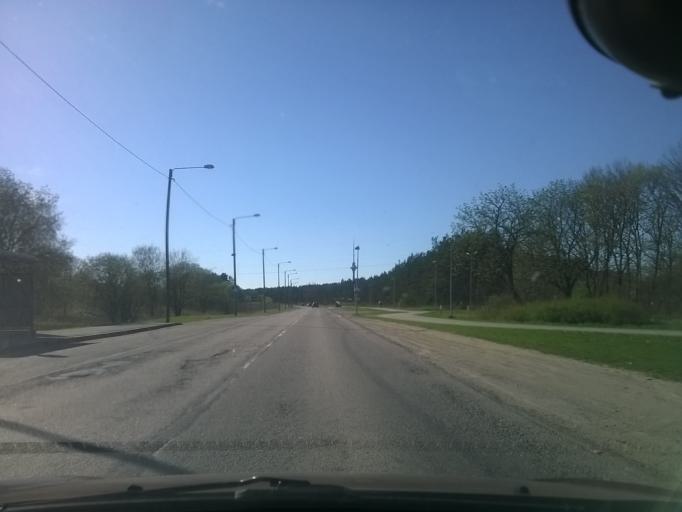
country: EE
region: Harju
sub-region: Joelaehtme vald
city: Loo
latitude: 59.4598
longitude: 24.9286
